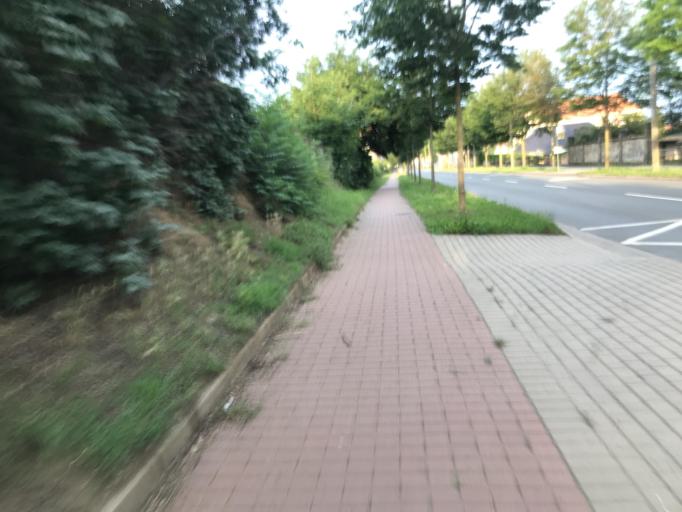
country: DE
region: Saxony-Anhalt
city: Quedlinburg
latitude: 51.7969
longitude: 11.1395
